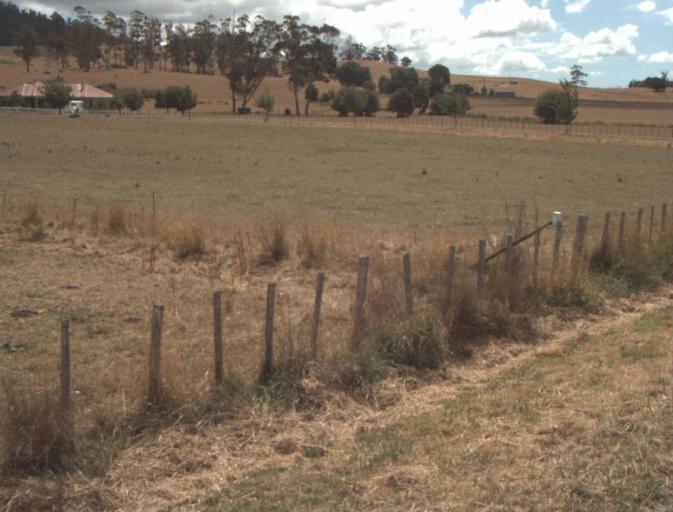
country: AU
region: Tasmania
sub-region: Launceston
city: Mayfield
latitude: -41.2335
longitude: 147.1254
